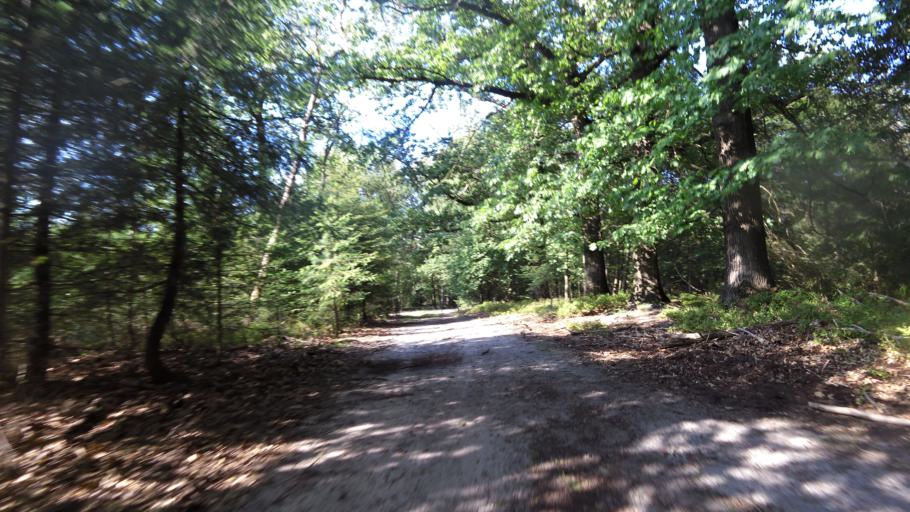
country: NL
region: Gelderland
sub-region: Gemeente Apeldoorn
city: Beekbergen
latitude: 52.1243
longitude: 5.9411
